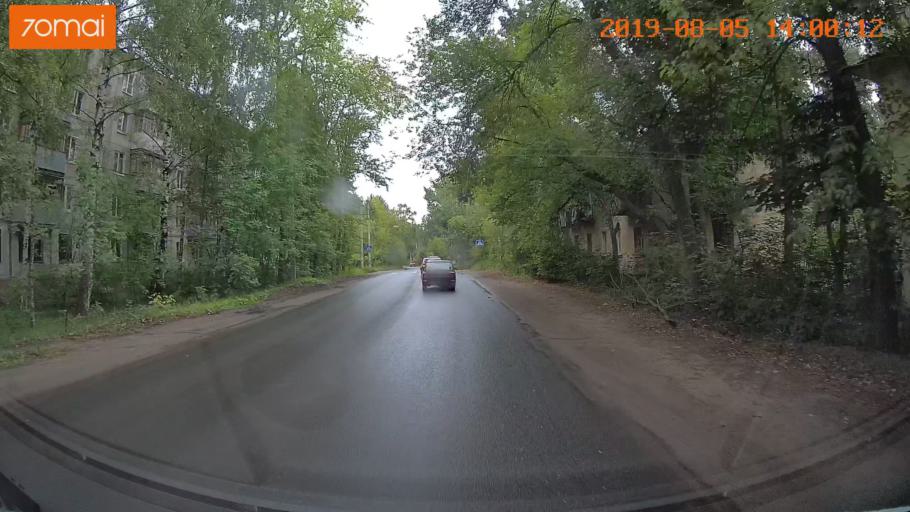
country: RU
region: Ivanovo
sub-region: Gorod Ivanovo
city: Ivanovo
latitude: 56.9880
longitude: 41.0176
